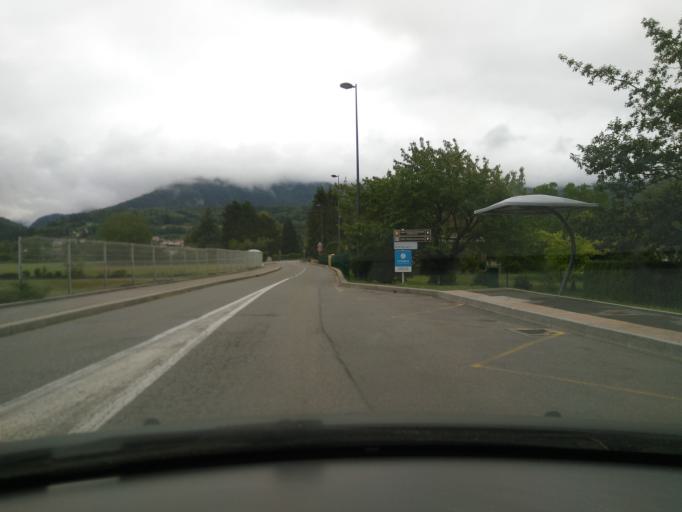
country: FR
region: Rhone-Alpes
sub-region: Departement de la Haute-Savoie
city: Amancy
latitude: 46.0650
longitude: 6.3641
